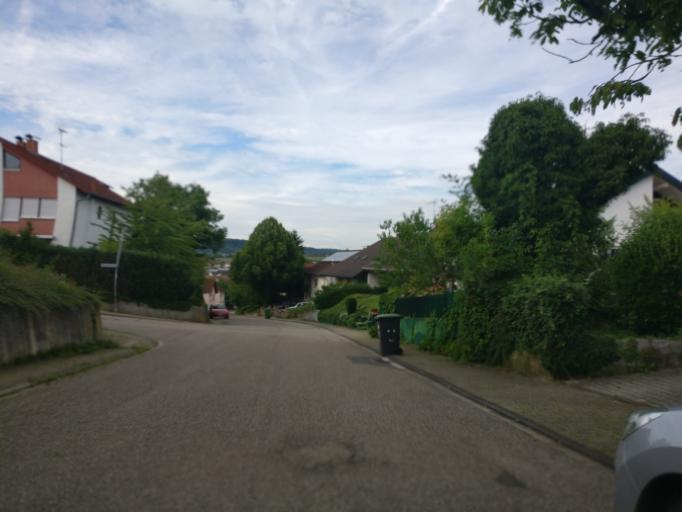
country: DE
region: Baden-Wuerttemberg
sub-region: Karlsruhe Region
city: Woessingen
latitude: 49.0102
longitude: 8.6022
